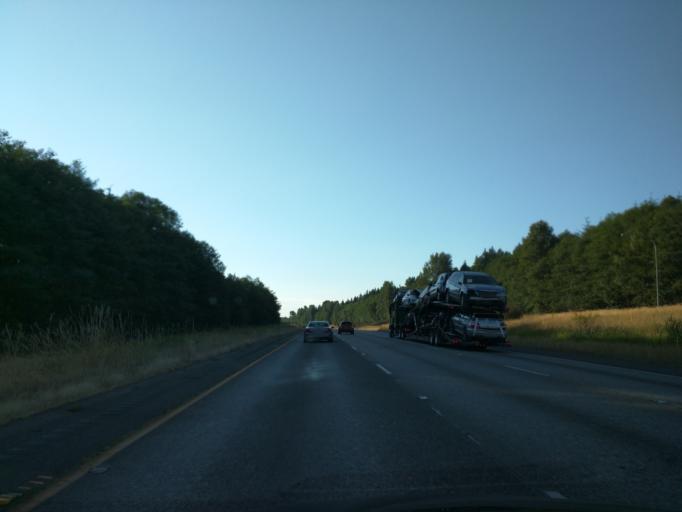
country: US
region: Washington
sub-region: Snohomish County
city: Bryant
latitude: 48.2574
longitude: -122.2576
